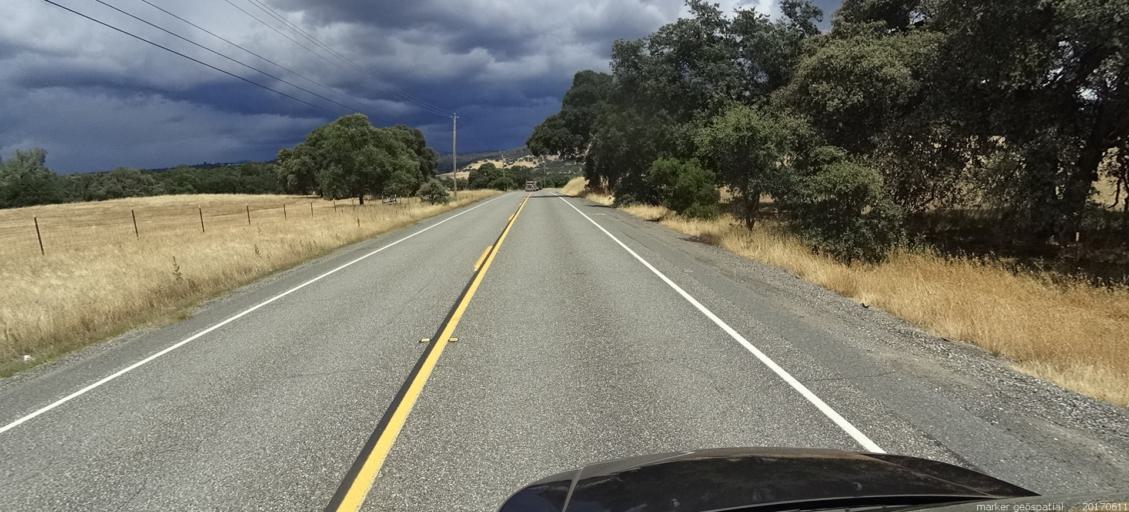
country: US
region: California
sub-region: Butte County
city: Paradise
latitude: 39.6522
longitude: -121.5964
